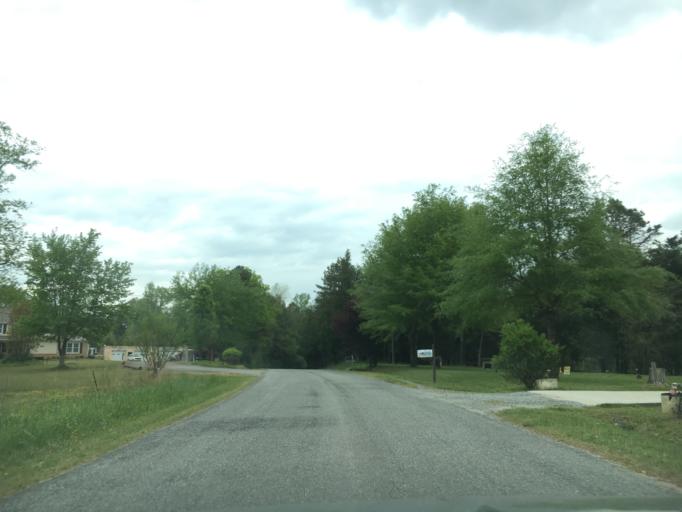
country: US
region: Virginia
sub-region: Halifax County
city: Halifax
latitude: 36.7983
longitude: -78.9332
